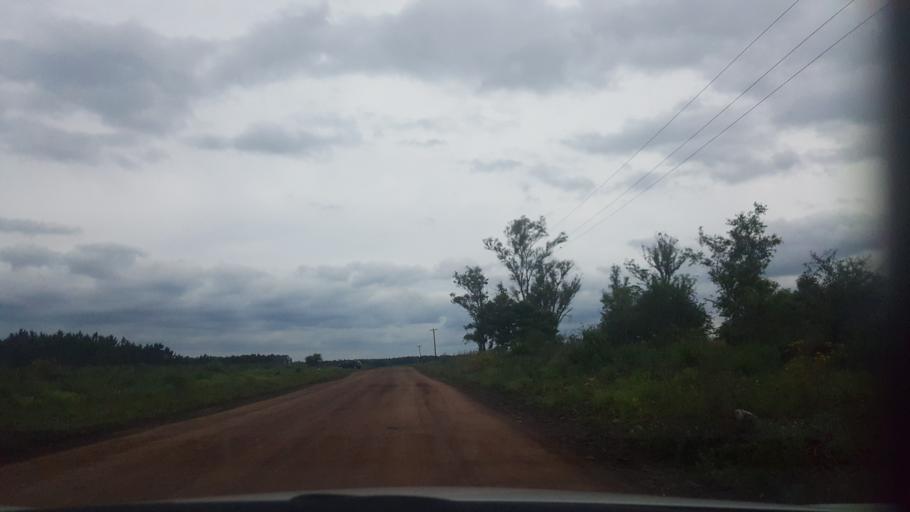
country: AR
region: Misiones
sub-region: Departamento de Candelaria
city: Candelaria
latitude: -27.4995
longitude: -55.7371
